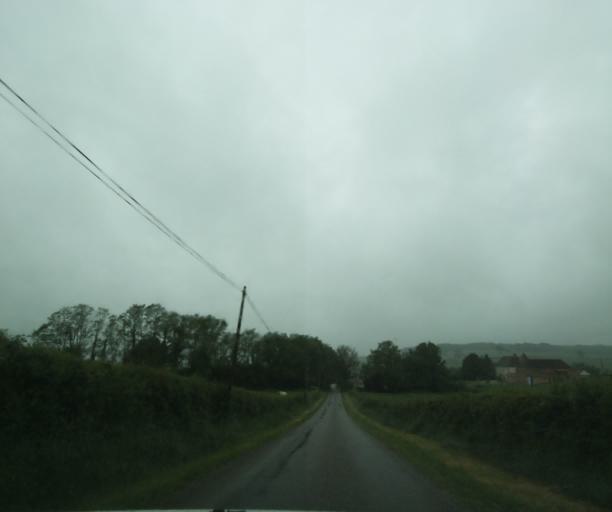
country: FR
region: Bourgogne
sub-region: Departement de Saone-et-Loire
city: Charolles
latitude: 46.4135
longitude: 4.2406
